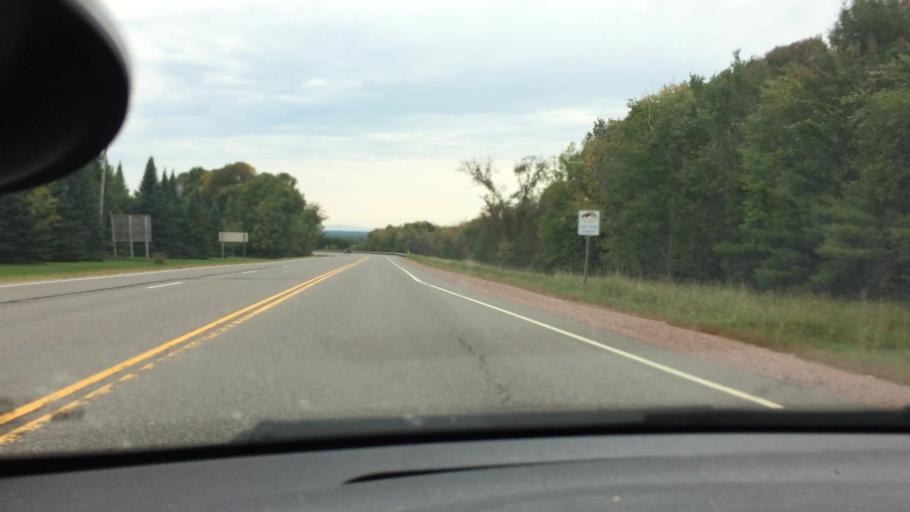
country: US
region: Wisconsin
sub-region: Clark County
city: Neillsville
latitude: 44.5650
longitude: -90.6601
